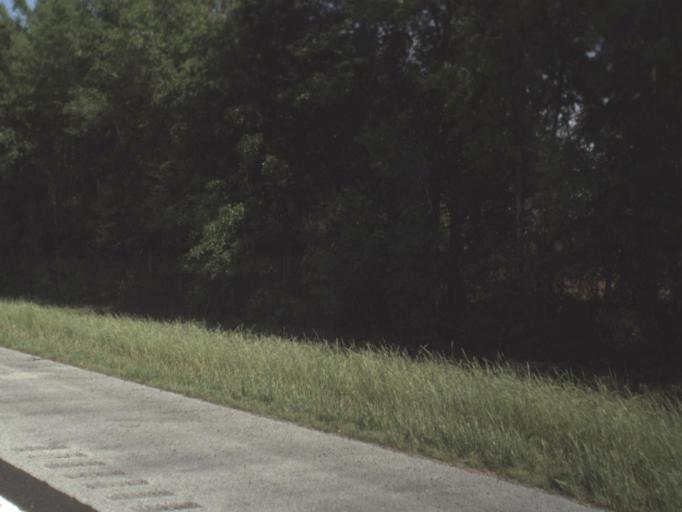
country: US
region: Florida
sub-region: Santa Rosa County
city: East Milton
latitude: 30.6267
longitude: -86.9388
